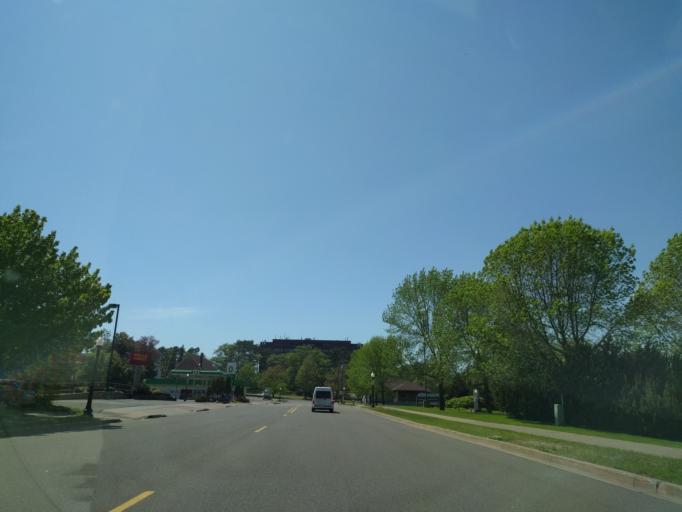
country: US
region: Michigan
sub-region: Marquette County
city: Marquette
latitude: 46.5566
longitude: -87.3937
